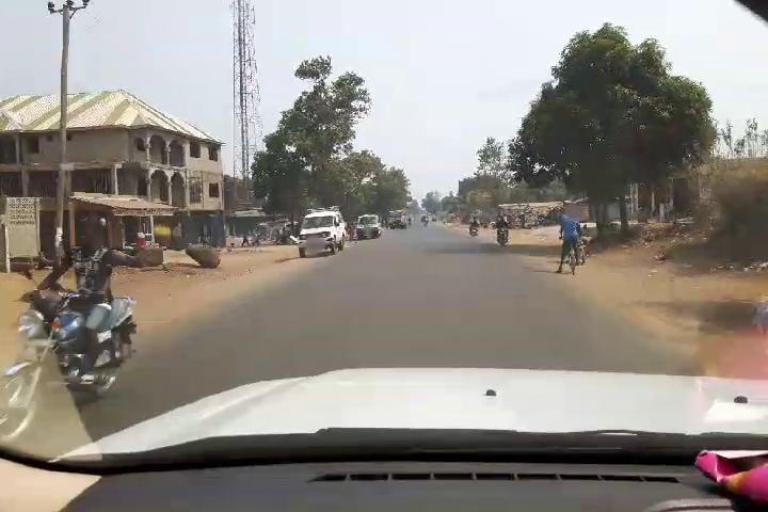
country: SL
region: Western Area
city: Waterloo
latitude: 8.3122
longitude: -13.0748
